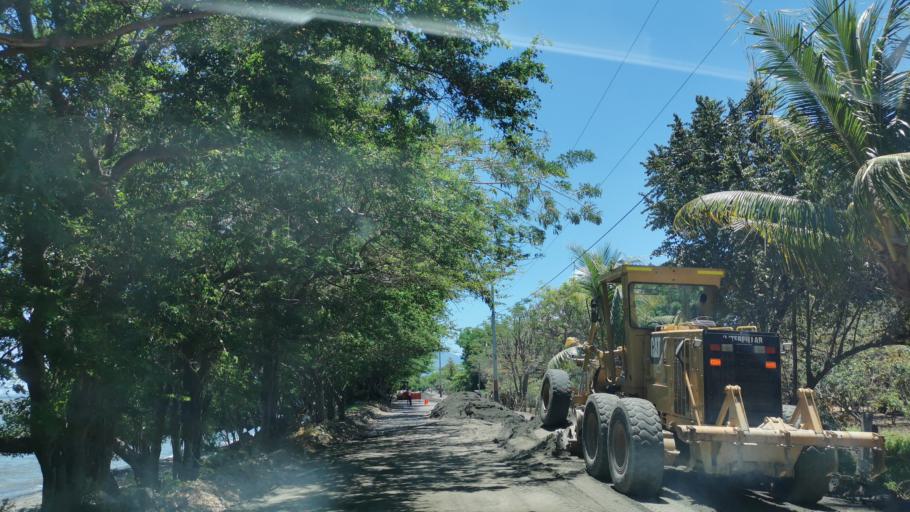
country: NI
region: Granada
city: Granada
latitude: 11.9884
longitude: -85.9387
